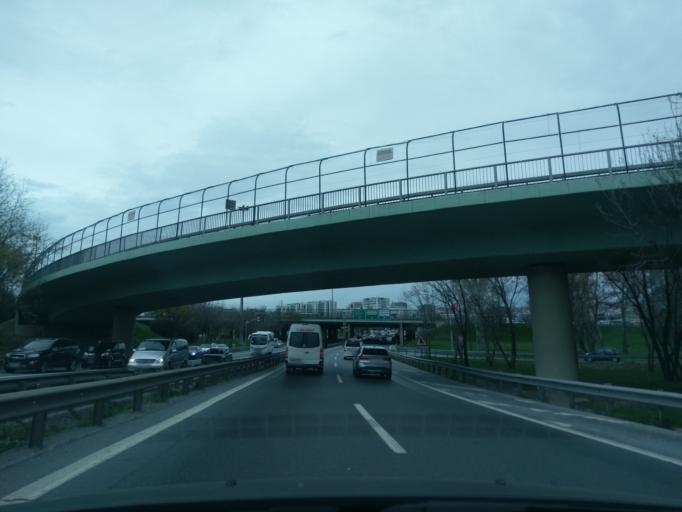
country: TR
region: Istanbul
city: Bahcelievler
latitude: 40.9918
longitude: 28.8184
